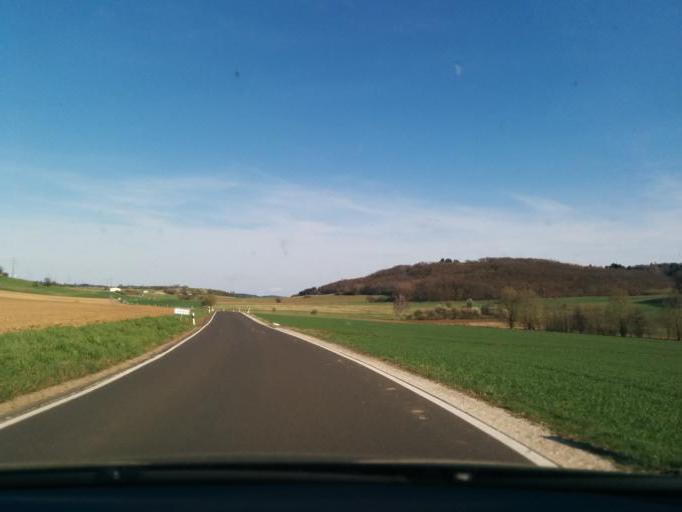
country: DE
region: Rheinland-Pfalz
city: Schlossbockelheim
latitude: 49.8155
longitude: 7.7581
